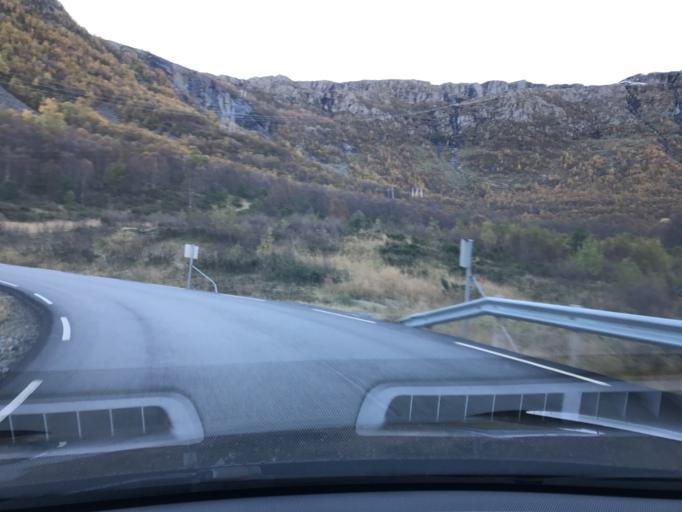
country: NO
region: Sogn og Fjordane
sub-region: Aurland
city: Aurlandsvangen
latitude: 60.8479
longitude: 7.3103
